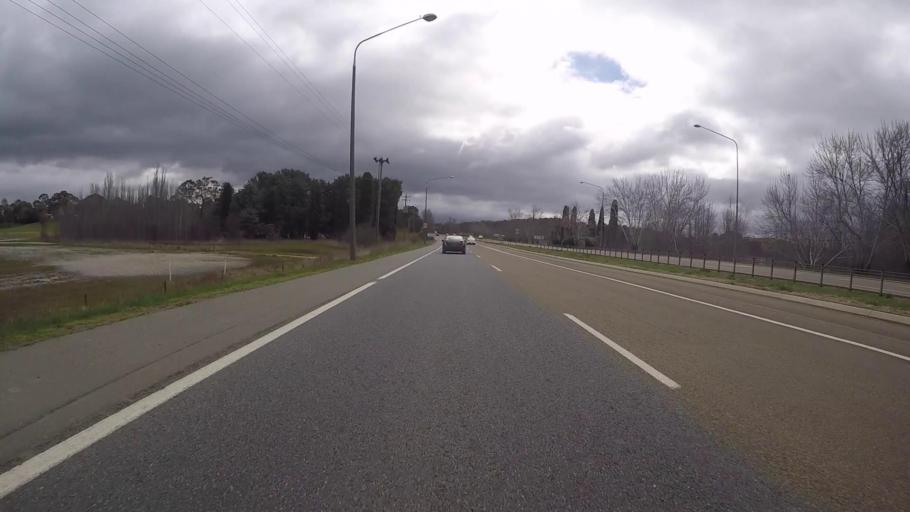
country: AU
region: Australian Capital Territory
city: Kaleen
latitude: -35.2191
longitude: 149.1184
